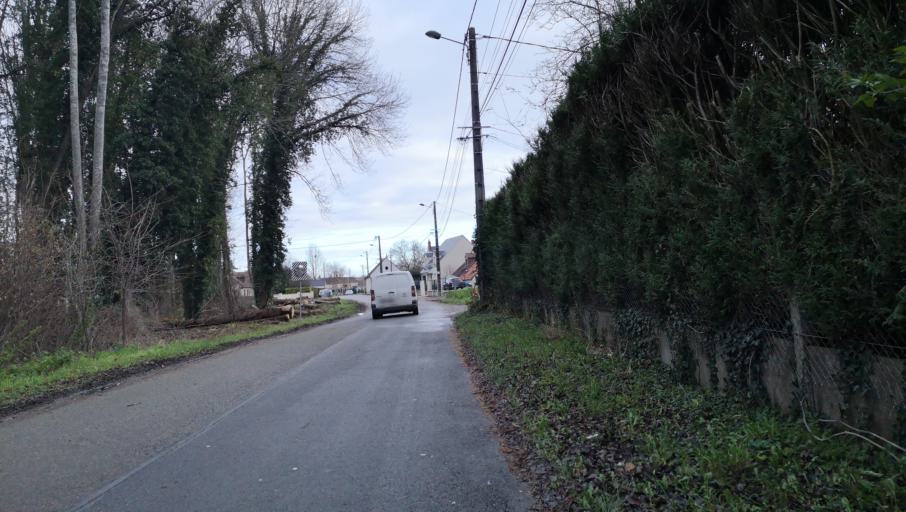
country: FR
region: Centre
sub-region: Departement du Loiret
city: Saint-Jean-de-Braye
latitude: 47.9096
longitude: 2.0002
